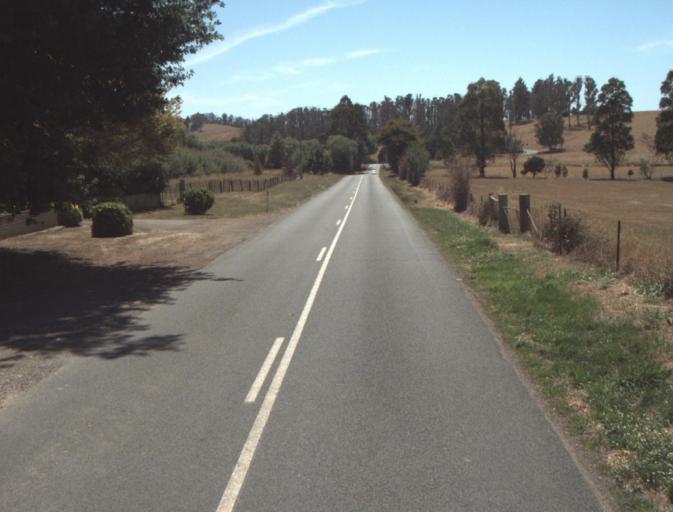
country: AU
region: Tasmania
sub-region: Launceston
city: Mayfield
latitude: -41.2637
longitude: 147.1350
